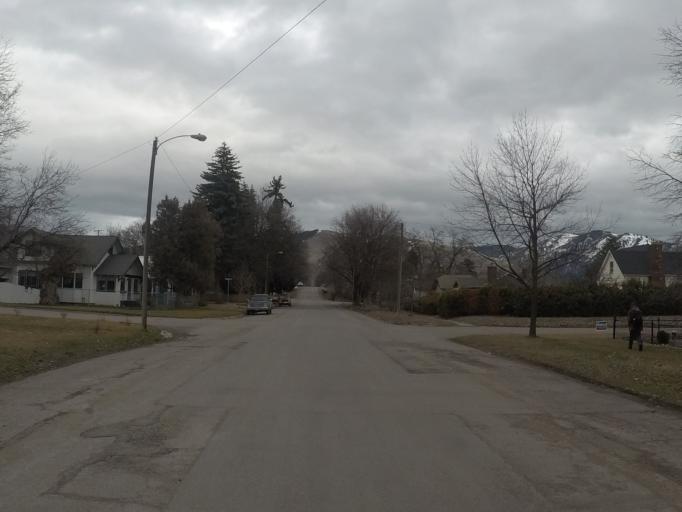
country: US
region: Montana
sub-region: Missoula County
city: Missoula
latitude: 46.8790
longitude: -114.0129
